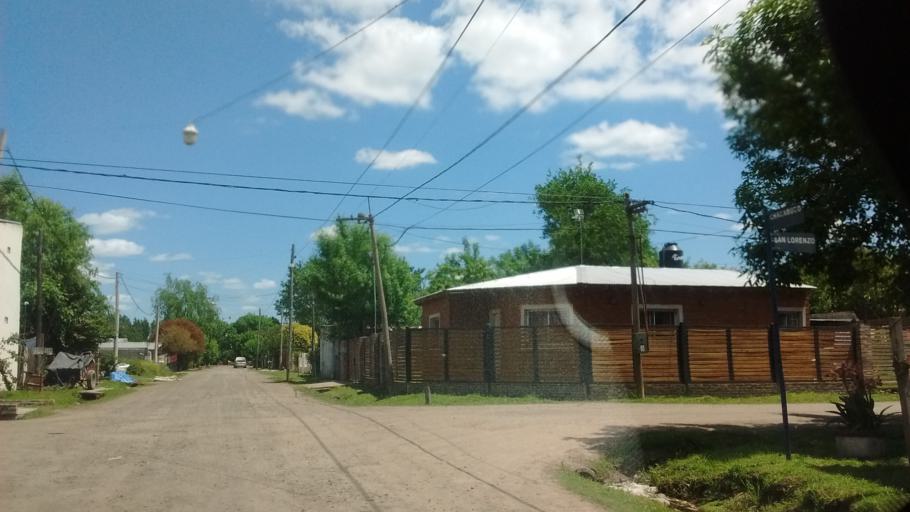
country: AR
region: Santa Fe
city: Funes
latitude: -32.8504
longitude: -60.7944
